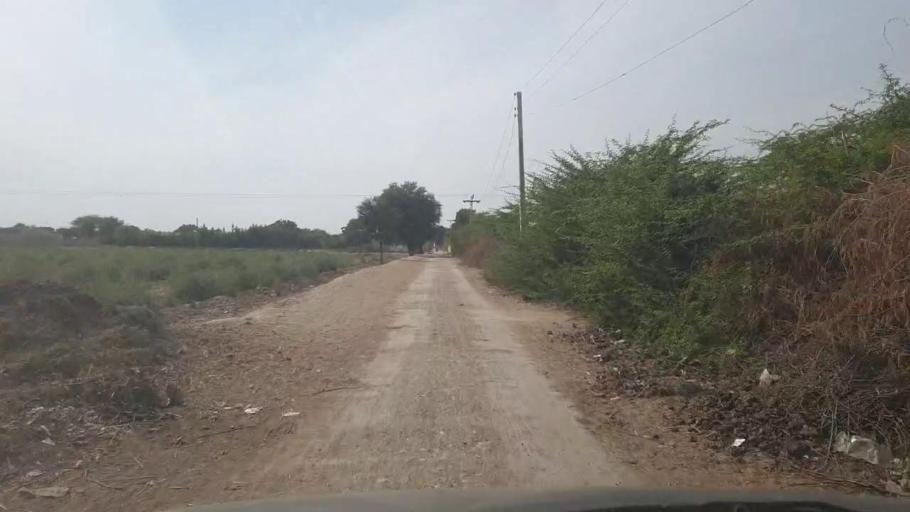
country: PK
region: Sindh
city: Kunri
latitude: 25.2383
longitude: 69.5923
